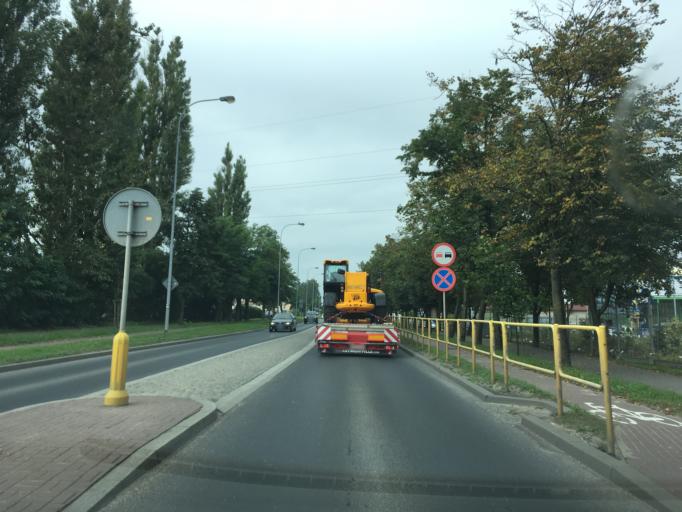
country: PL
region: Warmian-Masurian Voivodeship
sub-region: Powiat ostrodzki
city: Ostroda
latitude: 53.6899
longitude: 19.9830
